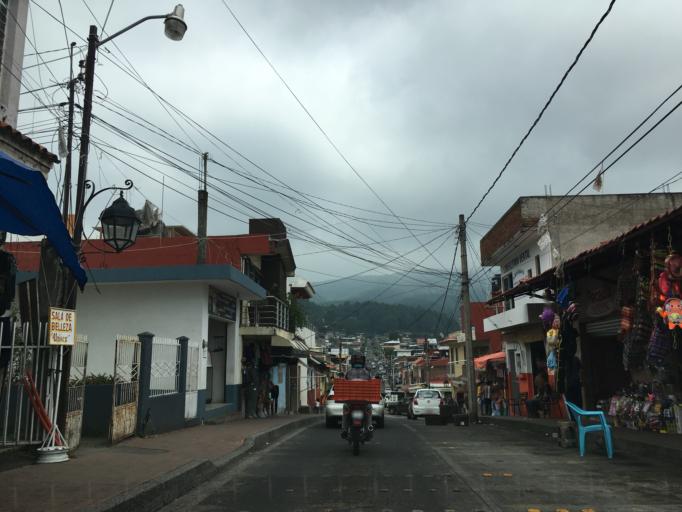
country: MX
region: Michoacan
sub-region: Uruapan
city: Uruapan
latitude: 19.4250
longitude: -102.0603
